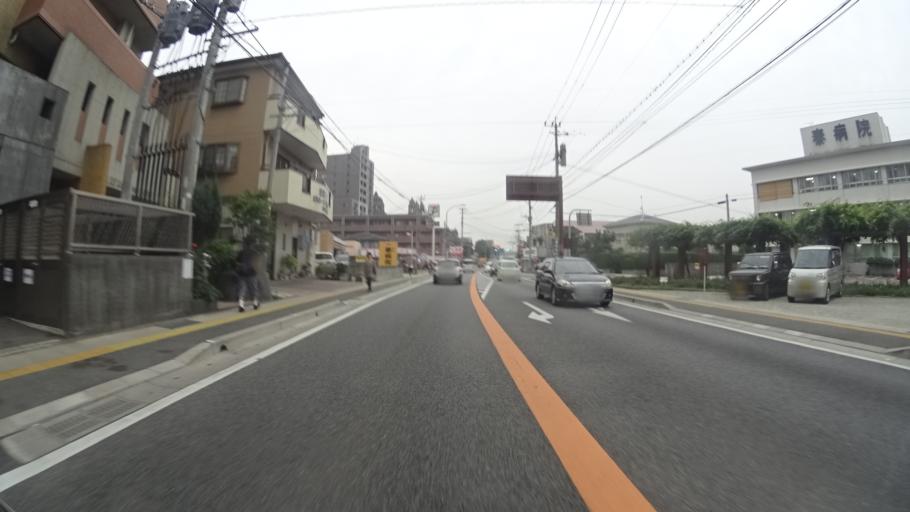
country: JP
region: Fukuoka
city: Onojo
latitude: 33.5402
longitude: 130.4742
